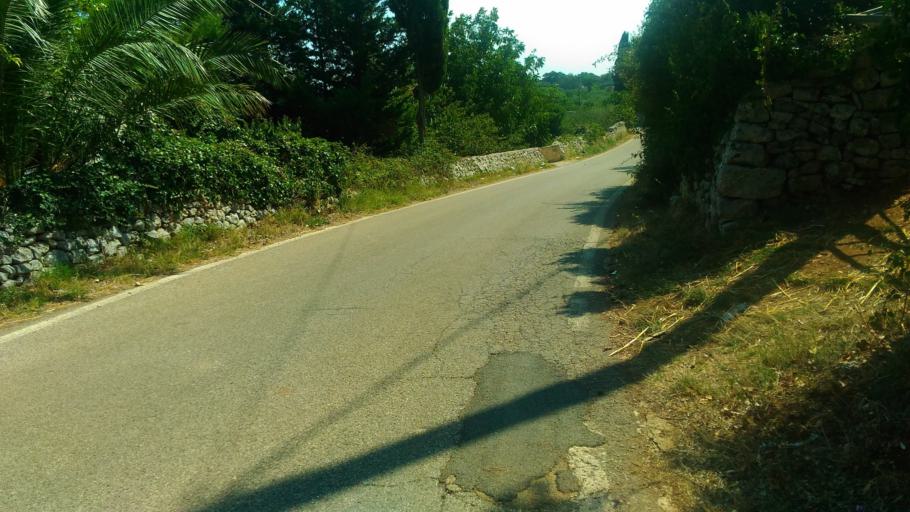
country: IT
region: Apulia
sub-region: Provincia di Bari
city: Locorotondo
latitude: 40.7516
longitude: 17.3578
